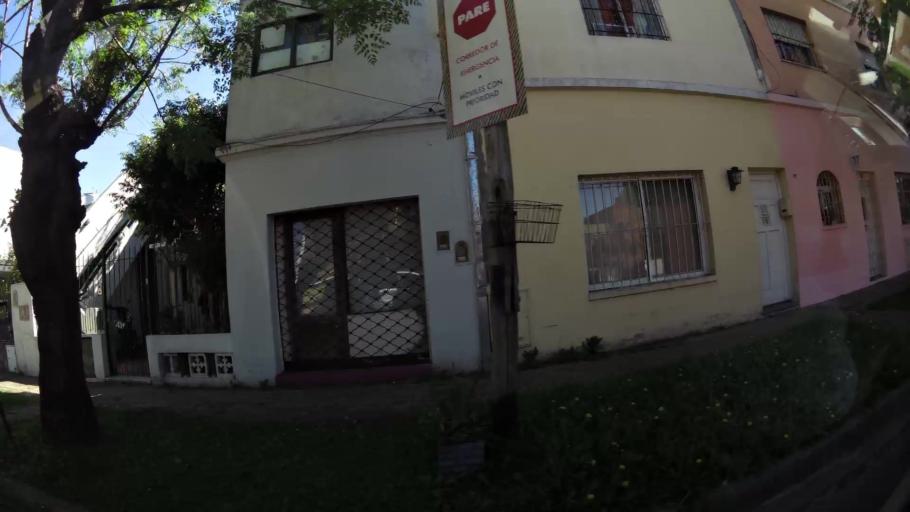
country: AR
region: Buenos Aires
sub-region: Partido de Vicente Lopez
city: Olivos
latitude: -34.5335
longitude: -58.5114
